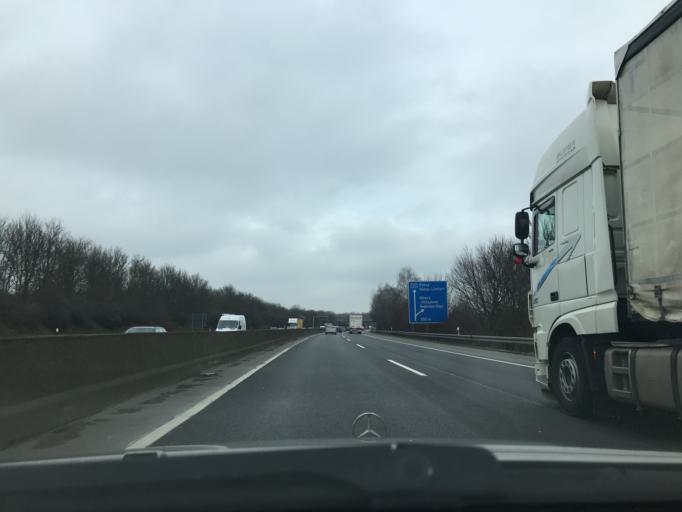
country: DE
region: North Rhine-Westphalia
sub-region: Regierungsbezirk Dusseldorf
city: Moers
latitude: 51.4512
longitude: 6.5938
